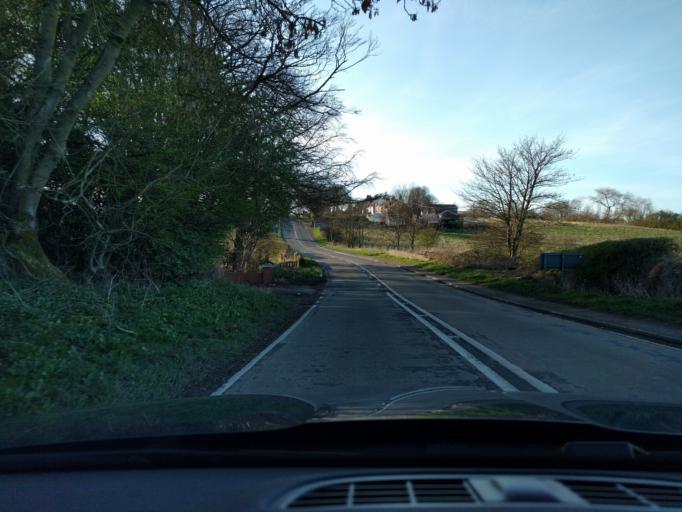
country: GB
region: England
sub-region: Northumberland
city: Pegswood
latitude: 55.1497
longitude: -1.6600
